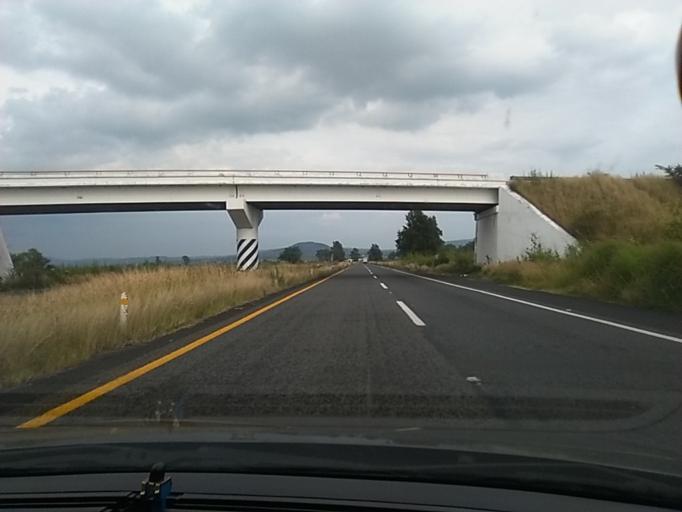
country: MX
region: Michoacan
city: Ecuandureo
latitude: 20.1749
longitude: -102.2278
